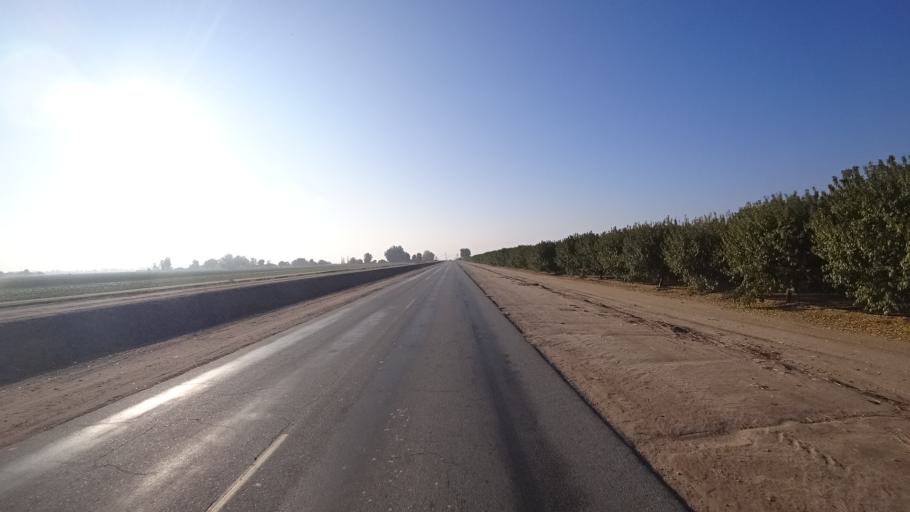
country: US
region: California
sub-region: Kern County
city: Greenfield
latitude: 35.2569
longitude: -118.9854
